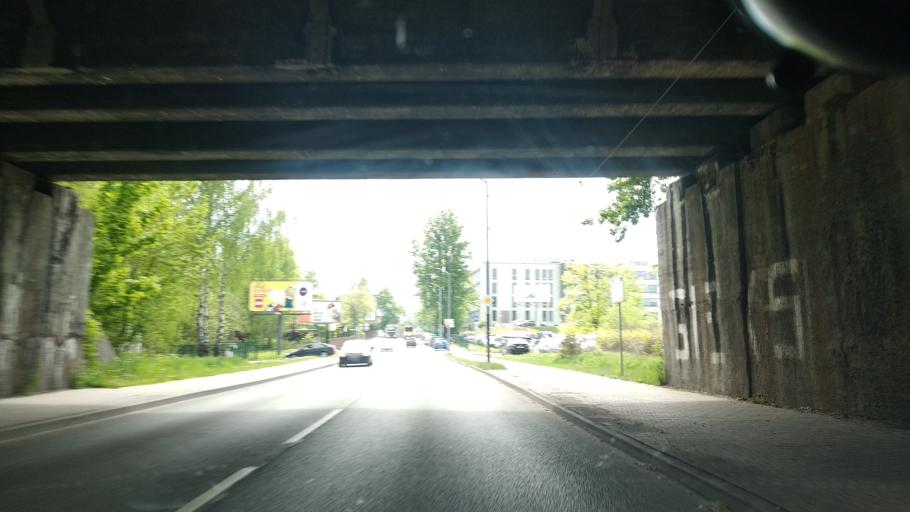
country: PL
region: Silesian Voivodeship
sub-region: Katowice
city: Katowice
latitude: 50.2381
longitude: 18.9795
